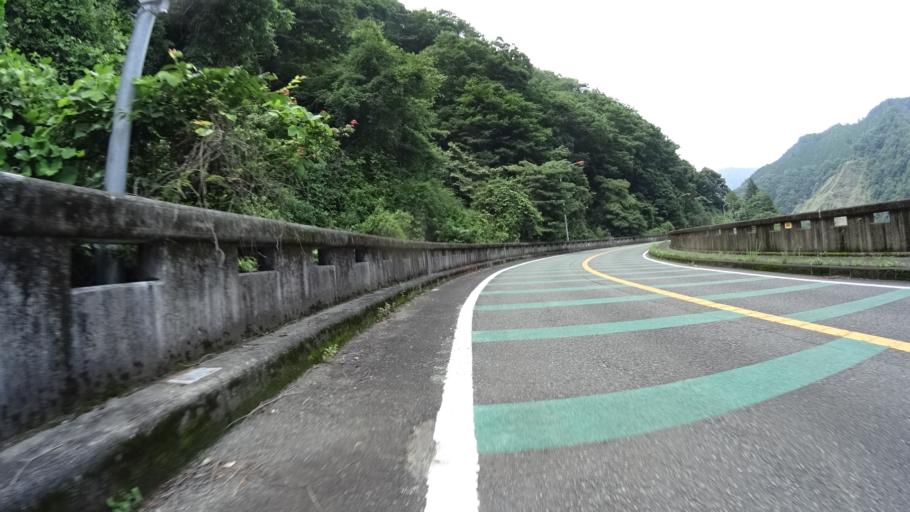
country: JP
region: Kanagawa
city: Hadano
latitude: 35.5049
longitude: 139.2294
